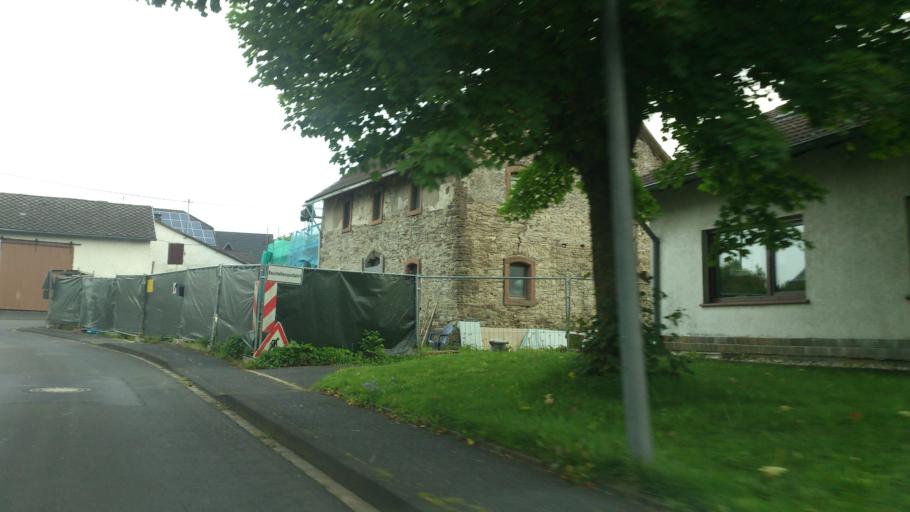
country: DE
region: Rheinland-Pfalz
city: Nohn
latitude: 50.3322
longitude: 6.7879
